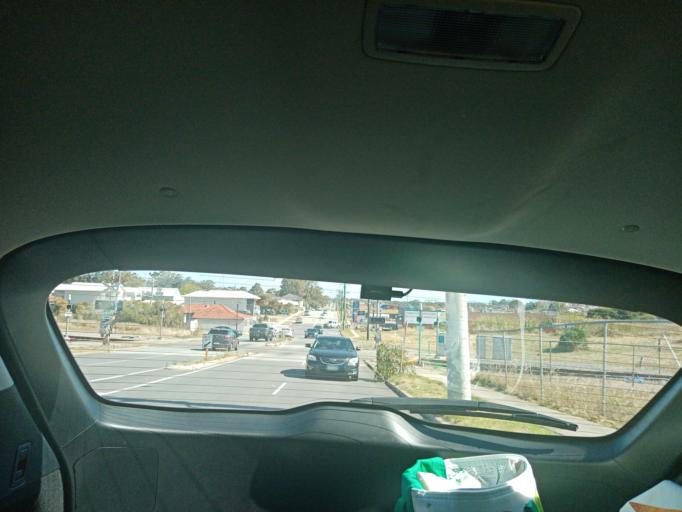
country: AU
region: Western Australia
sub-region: City of Cockburn
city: Spearwood
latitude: -32.1037
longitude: 115.7826
